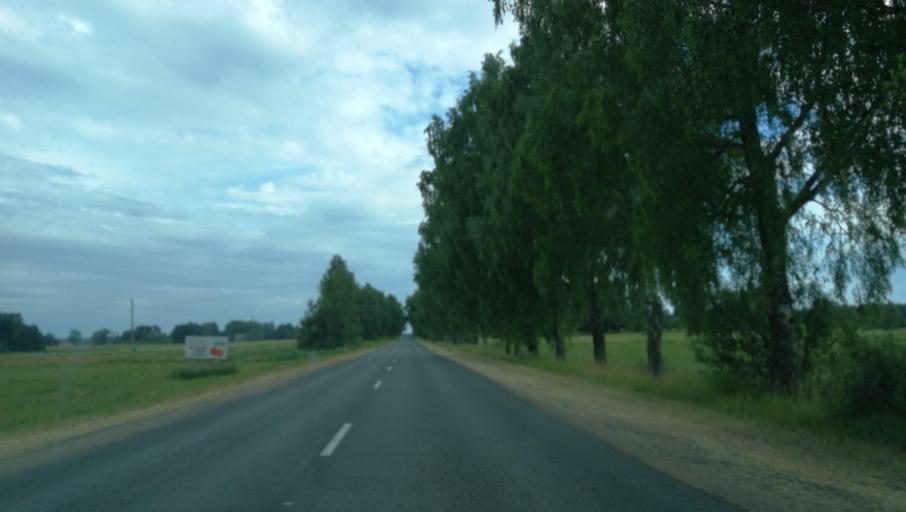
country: LV
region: Valmieras Rajons
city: Valmiera
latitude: 57.6185
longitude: 25.4521
